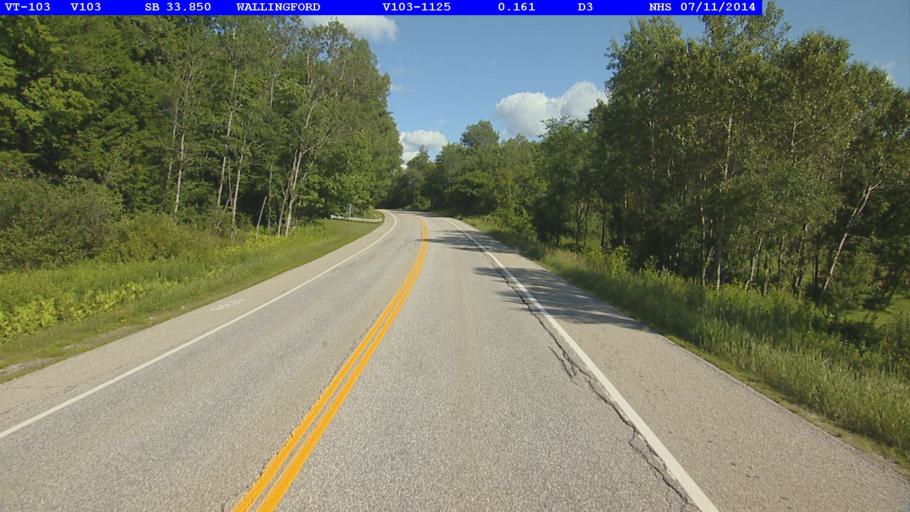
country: US
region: Vermont
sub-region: Rutland County
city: Rutland
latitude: 43.4528
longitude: -72.8750
